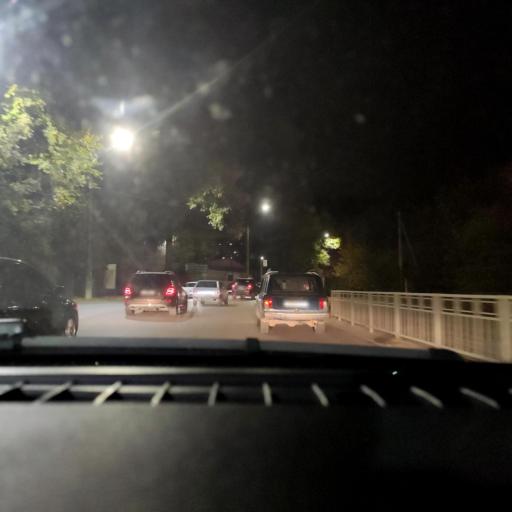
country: RU
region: Voronezj
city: Maslovka
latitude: 51.6309
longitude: 39.2618
